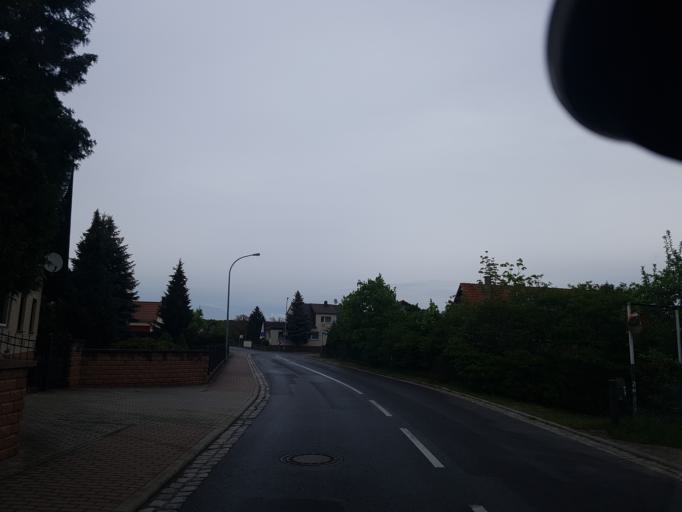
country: DE
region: Brandenburg
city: Heinersbruck
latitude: 51.6852
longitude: 14.4760
